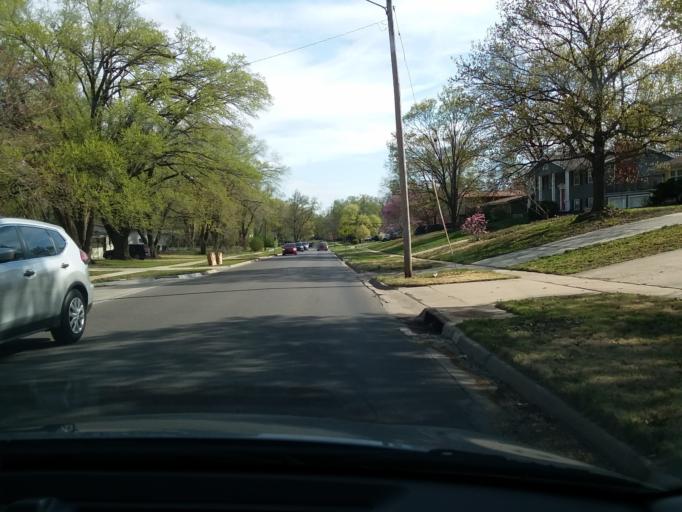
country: US
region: Kansas
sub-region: Douglas County
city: Lawrence
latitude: 38.9691
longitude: -95.2748
